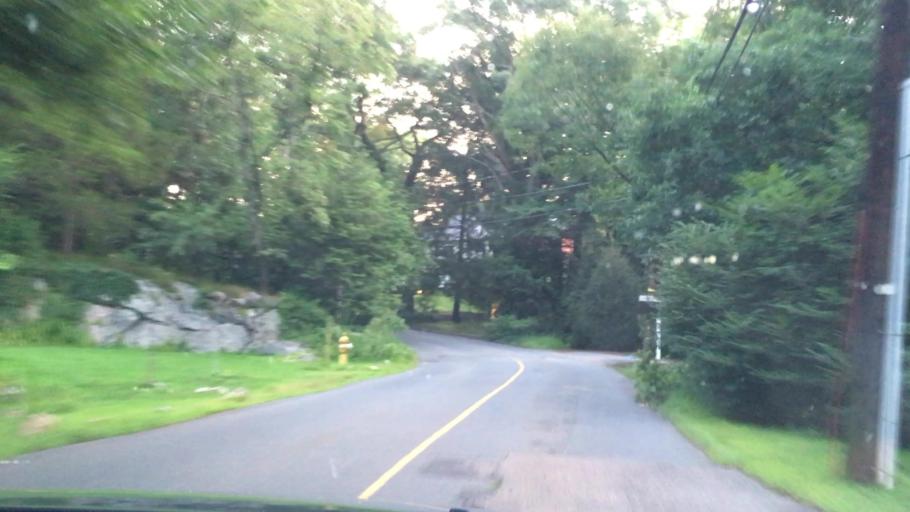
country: US
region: Massachusetts
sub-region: Norfolk County
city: Wellesley
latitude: 42.3282
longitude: -71.2743
